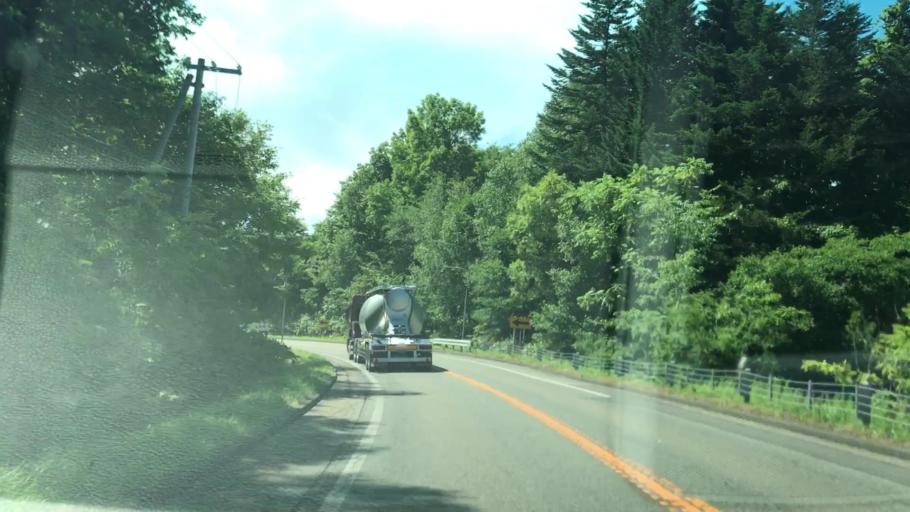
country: JP
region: Hokkaido
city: Shimo-furano
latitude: 42.8919
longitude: 142.4350
